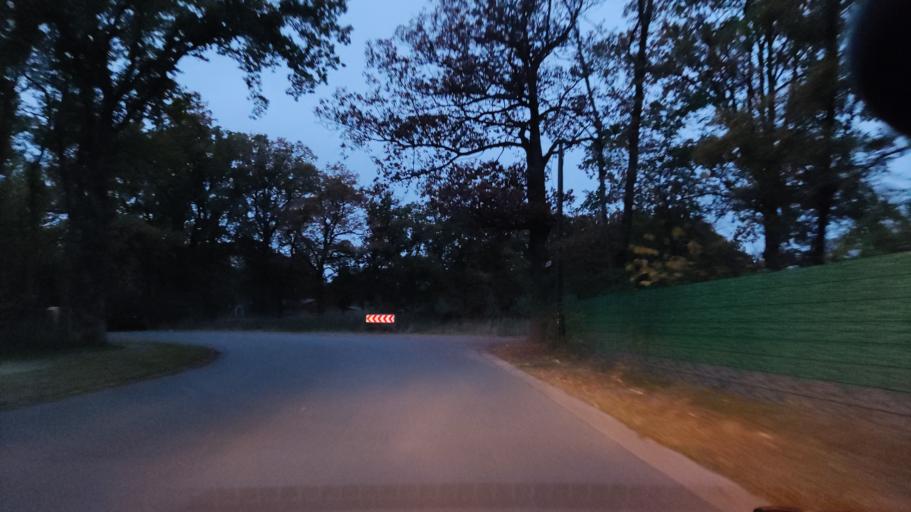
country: DE
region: Lower Saxony
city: Munster
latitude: 53.0157
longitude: 10.0892
